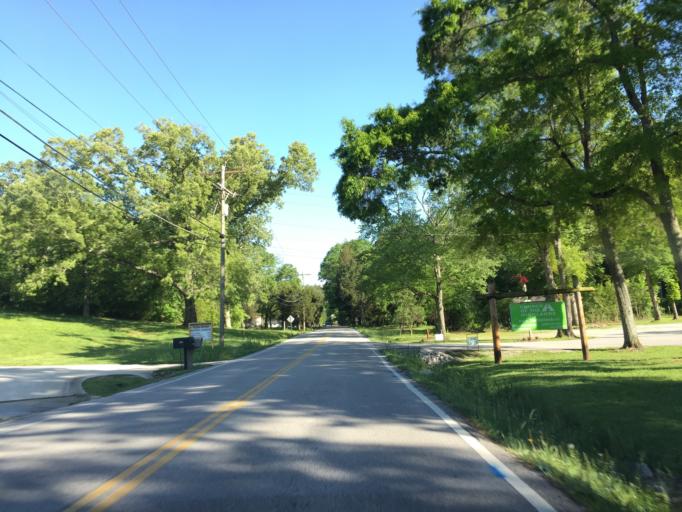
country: US
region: Tennessee
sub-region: Hamilton County
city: Harrison
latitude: 35.1356
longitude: -85.1160
